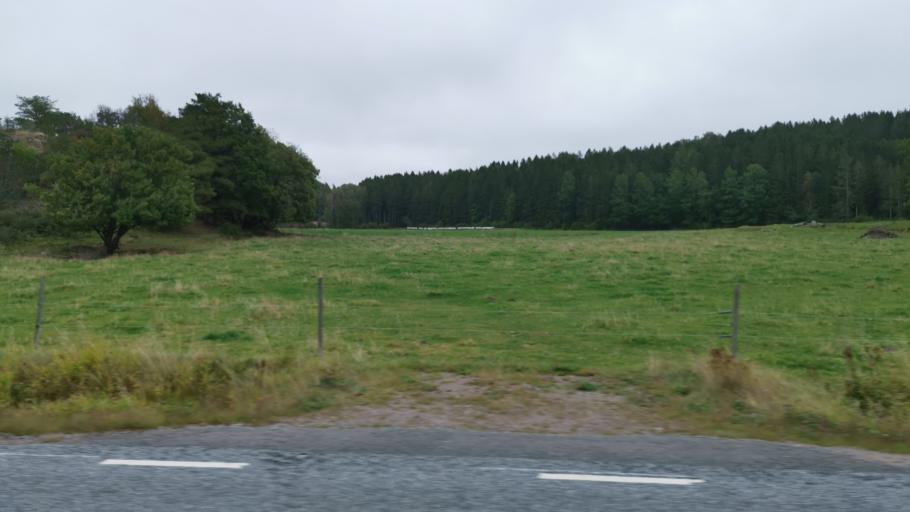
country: SE
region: Vaestra Goetaland
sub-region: Tanums Kommun
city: Tanumshede
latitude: 58.6374
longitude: 11.3427
